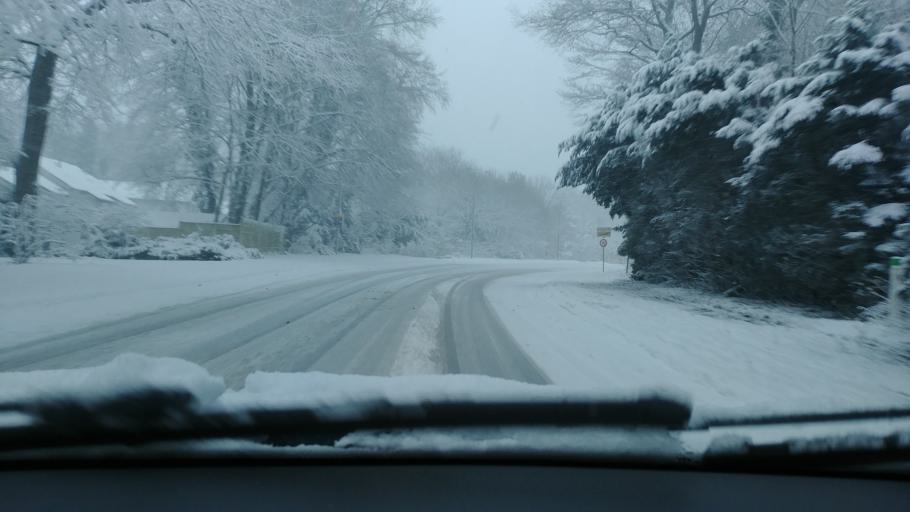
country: DE
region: North Rhine-Westphalia
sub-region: Regierungsbezirk Koln
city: Bergisch Gladbach
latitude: 50.9519
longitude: 7.1288
